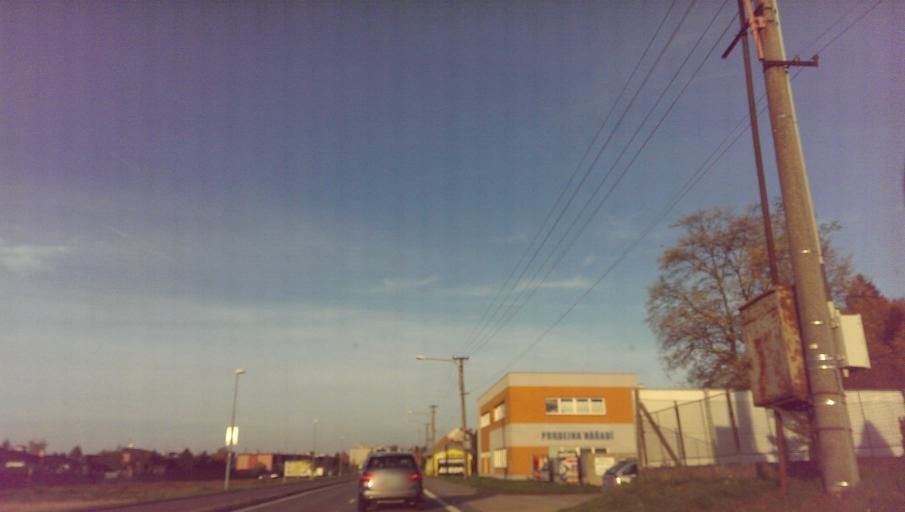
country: CZ
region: Zlin
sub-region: Okres Uherske Hradiste
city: Uherske Hradiste
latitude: 49.0805
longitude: 17.4876
